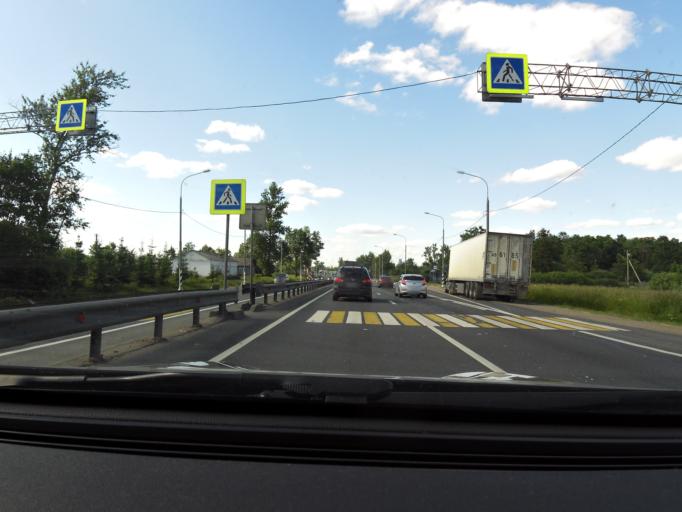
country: RU
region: Novgorod
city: Chudovo
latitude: 59.1293
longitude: 31.6344
